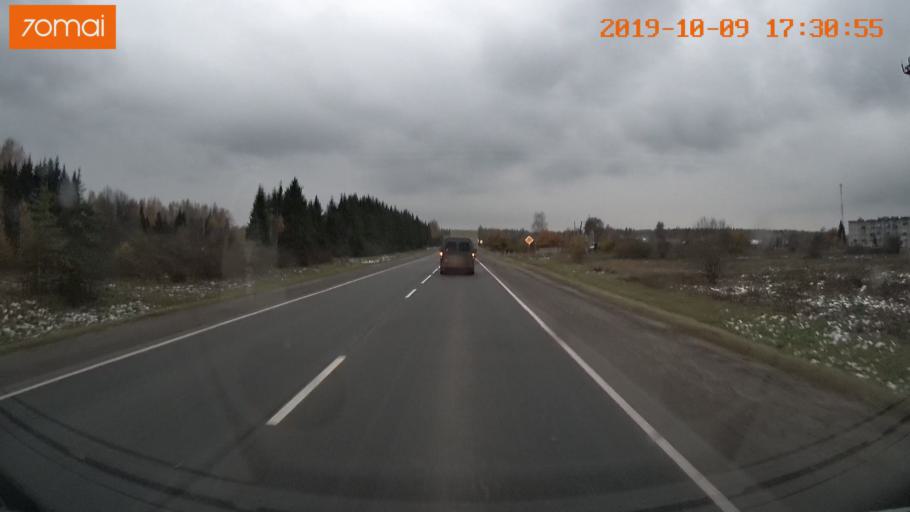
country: RU
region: Ivanovo
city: Bogorodskoye
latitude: 57.1391
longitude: 41.0444
